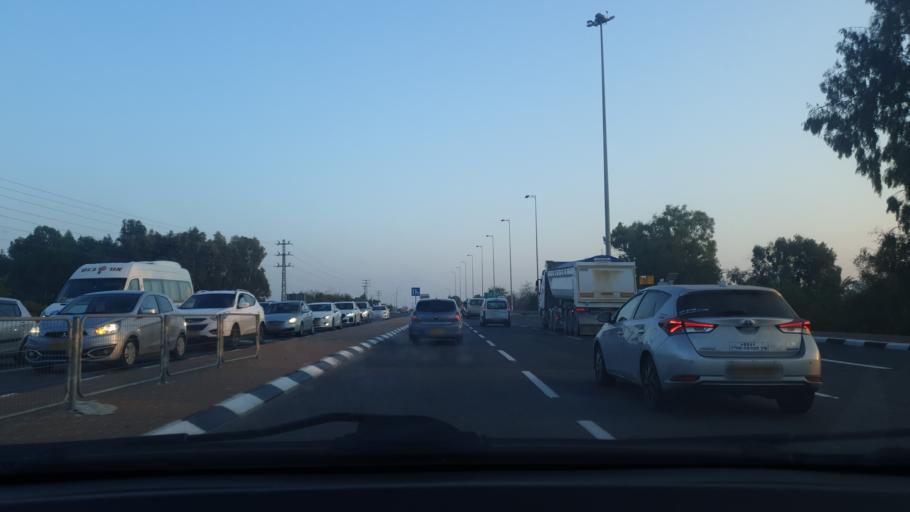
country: IL
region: Central District
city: Ramla
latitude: 31.9512
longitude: 34.8566
